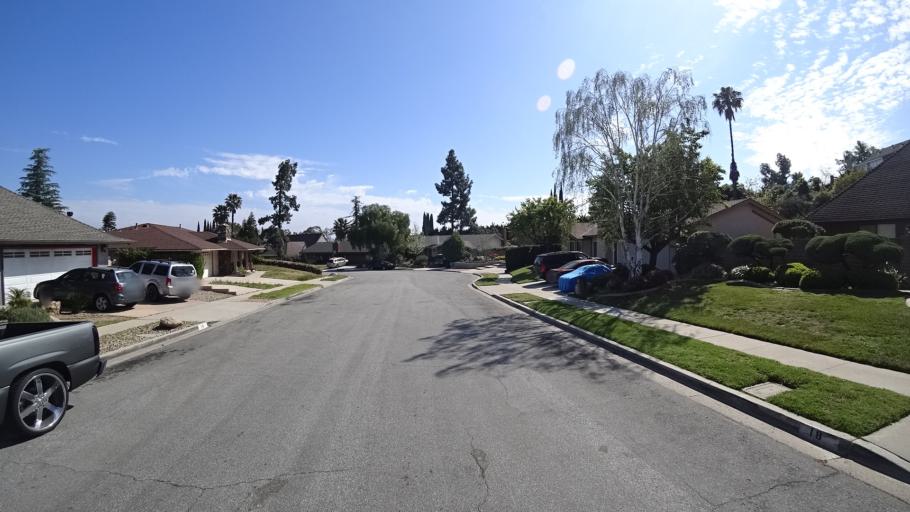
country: US
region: California
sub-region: Ventura County
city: Casa Conejo
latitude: 34.1782
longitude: -118.9251
